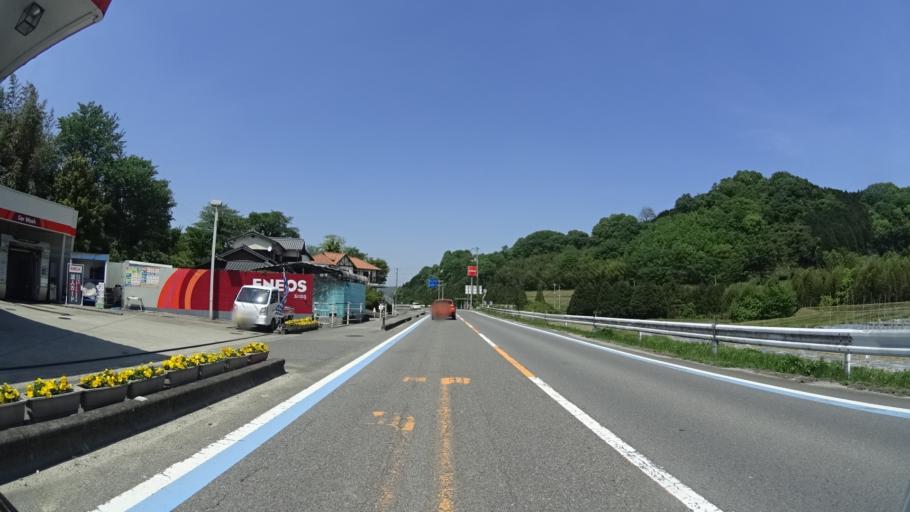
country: JP
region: Ehime
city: Hojo
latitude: 34.0038
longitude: 132.9382
